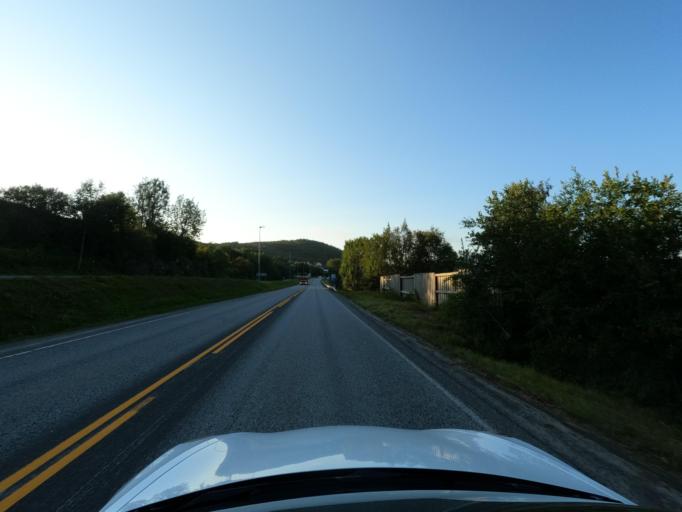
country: NO
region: Troms
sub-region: Harstad
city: Harstad
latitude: 68.7679
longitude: 16.5589
